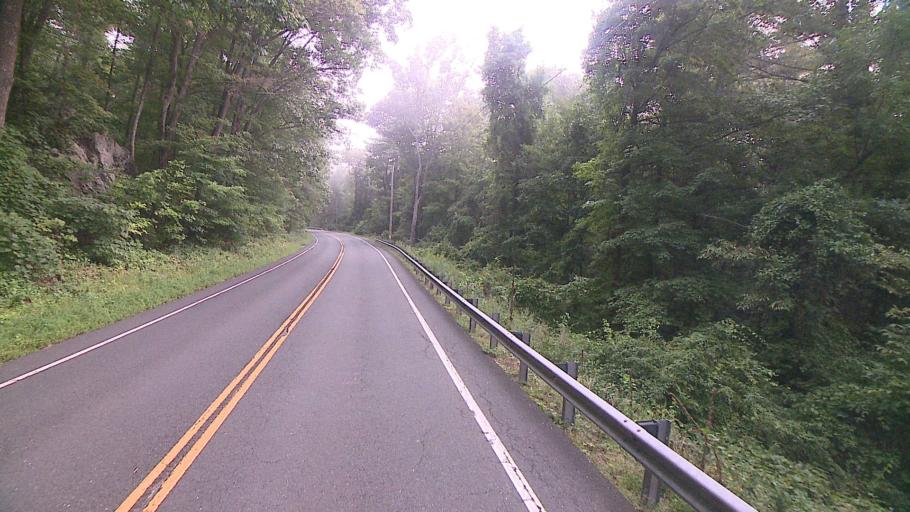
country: US
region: Connecticut
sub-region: Litchfield County
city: Canaan
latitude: 41.9190
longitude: -73.3657
